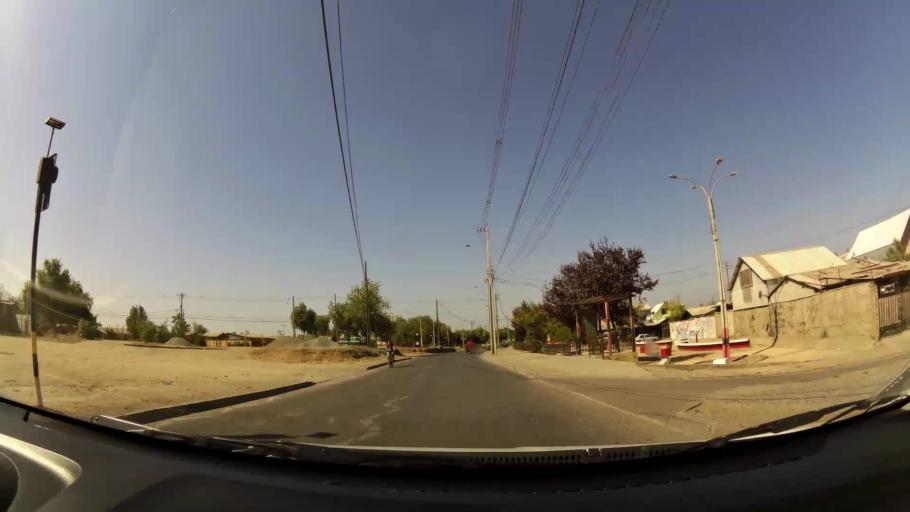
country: CL
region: Maule
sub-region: Provincia de Talca
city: Talca
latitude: -35.4000
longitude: -71.6523
